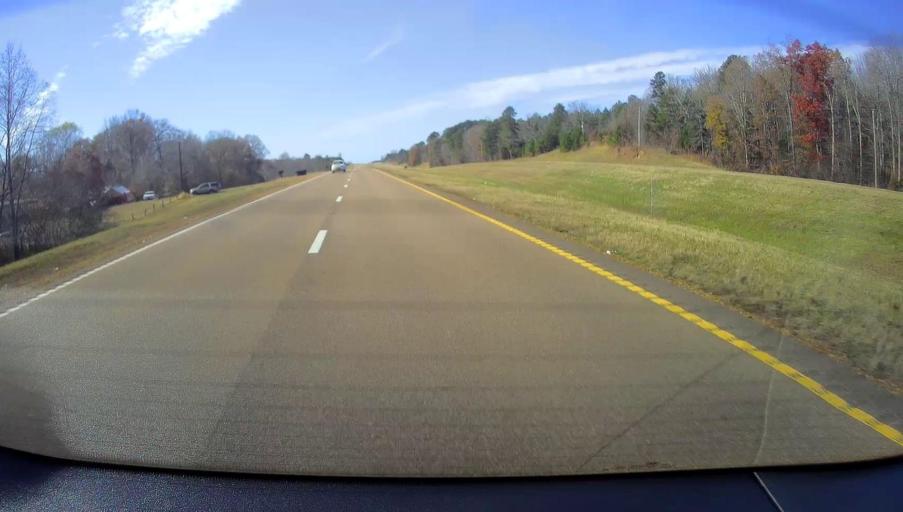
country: US
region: Mississippi
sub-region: Benton County
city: Ashland
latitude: 34.9513
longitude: -89.0683
